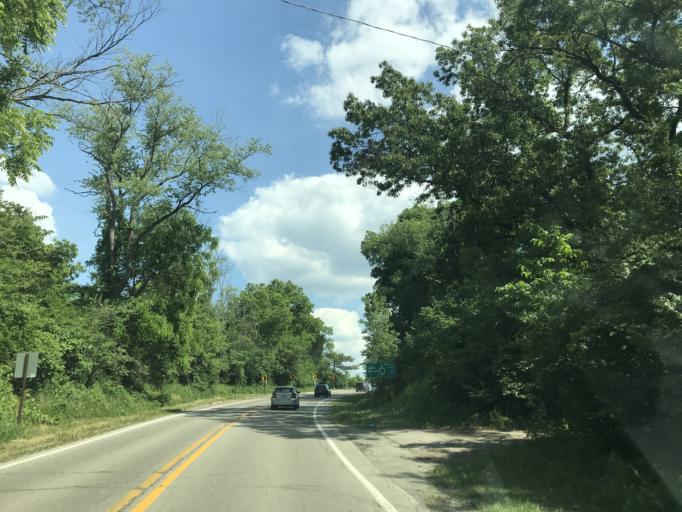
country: US
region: Michigan
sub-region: Washtenaw County
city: Ypsilanti
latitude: 42.2776
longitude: -83.6389
